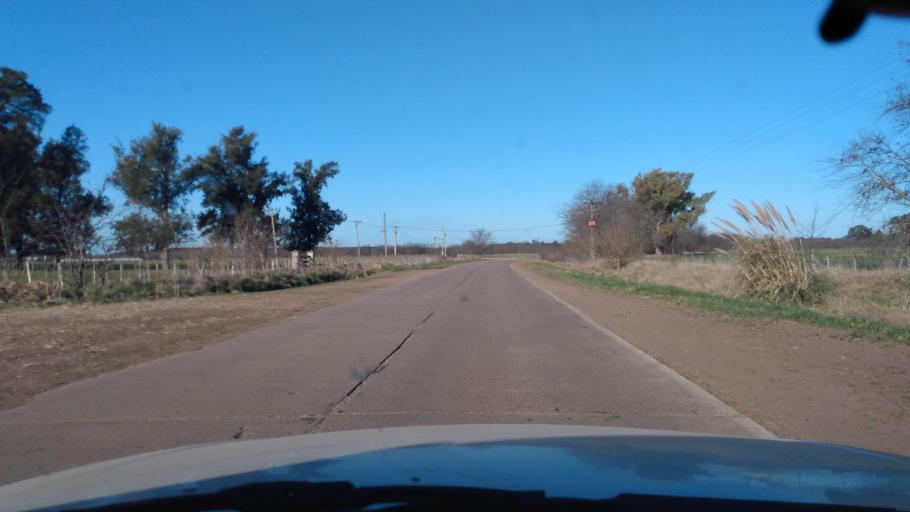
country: AR
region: Buenos Aires
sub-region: Partido de Mercedes
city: Mercedes
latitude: -34.6145
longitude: -59.2675
